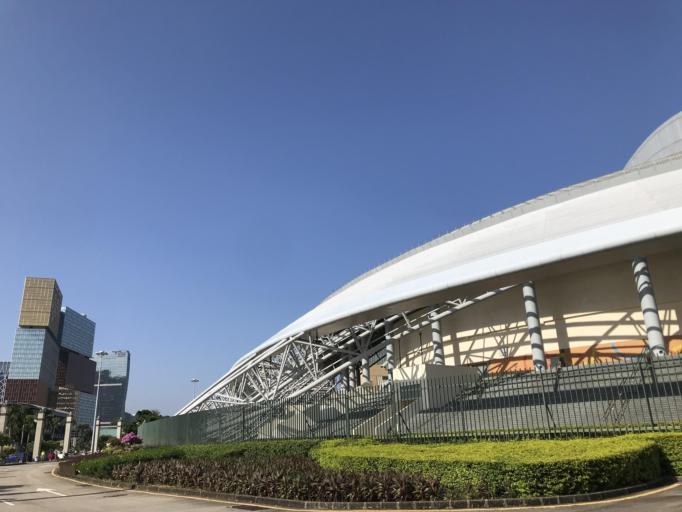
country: MO
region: Macau
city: Macau
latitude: 22.1394
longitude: 113.5692
